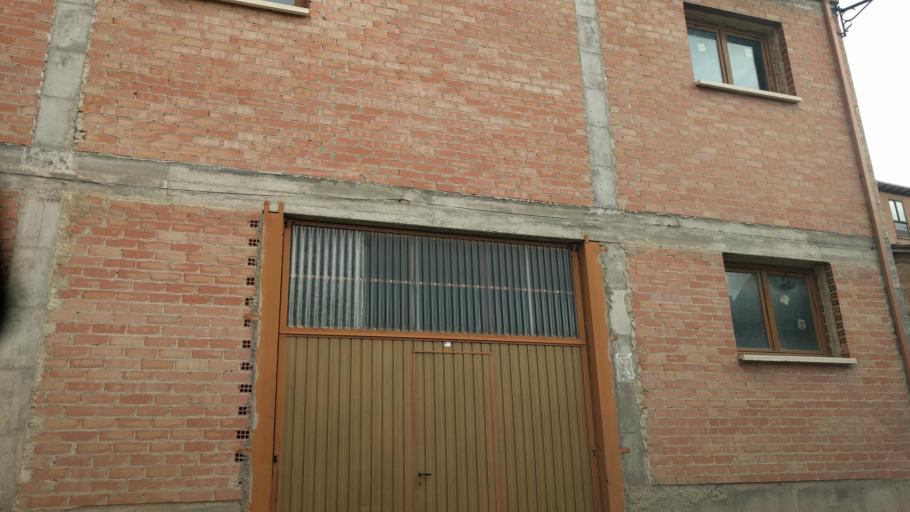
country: ES
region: La Rioja
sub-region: Provincia de La Rioja
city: San Vicente de la Sonsierra
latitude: 42.5617
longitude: -2.7593
